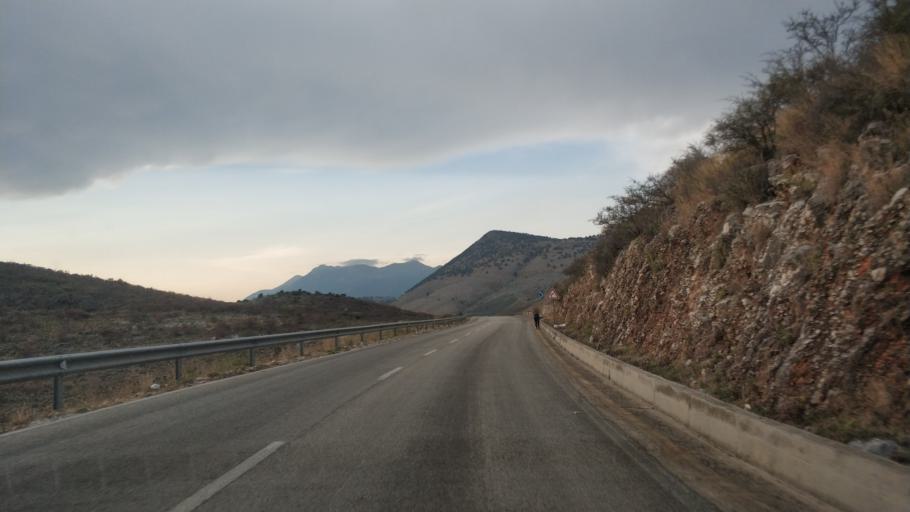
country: AL
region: Vlore
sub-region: Rrethi i Vlores
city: Himare
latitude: 40.0496
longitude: 19.8045
